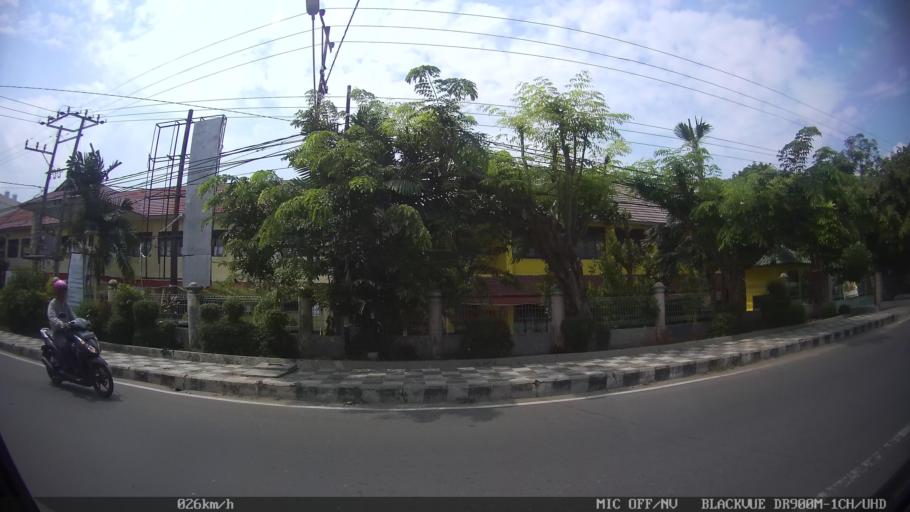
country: ID
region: Lampung
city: Bandarlampung
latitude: -5.4344
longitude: 105.2603
